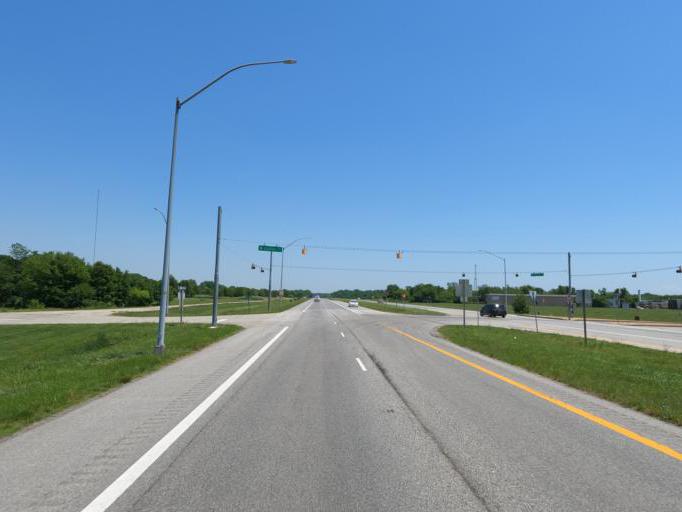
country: US
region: Maryland
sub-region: Caroline County
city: Denton
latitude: 38.8971
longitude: -75.8539
